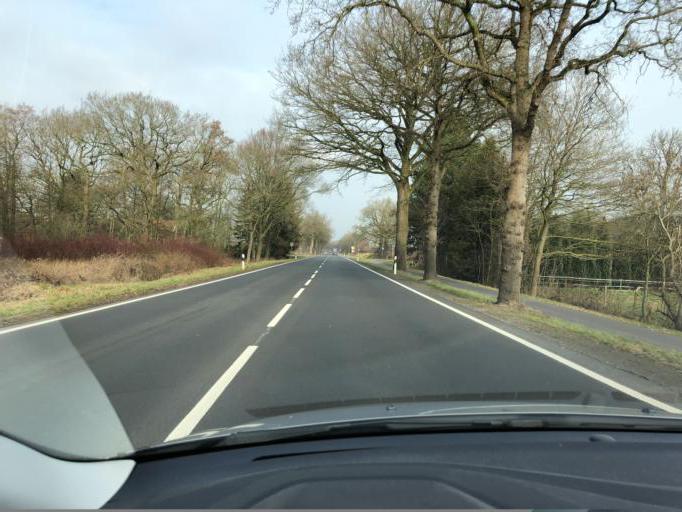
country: DE
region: Lower Saxony
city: Hesel
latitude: 53.3521
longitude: 7.6017
